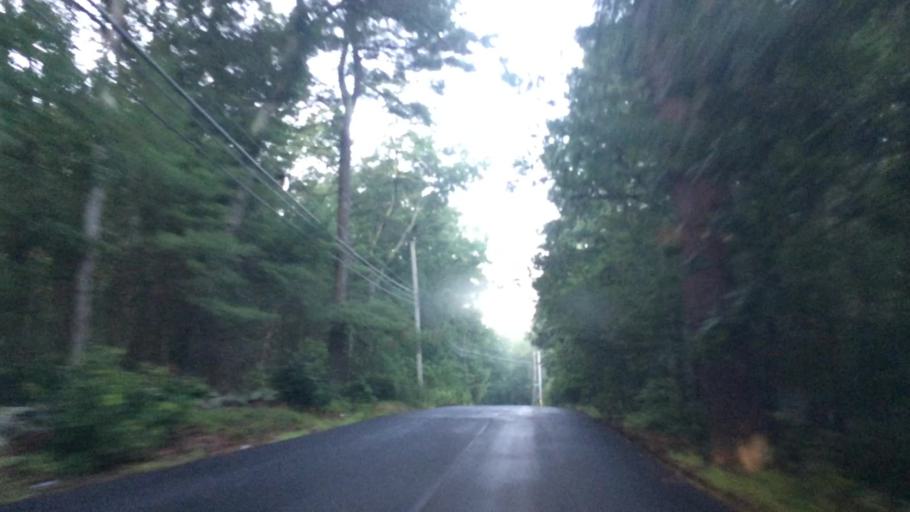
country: US
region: Massachusetts
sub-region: Middlesex County
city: North Reading
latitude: 42.6159
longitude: -71.0927
